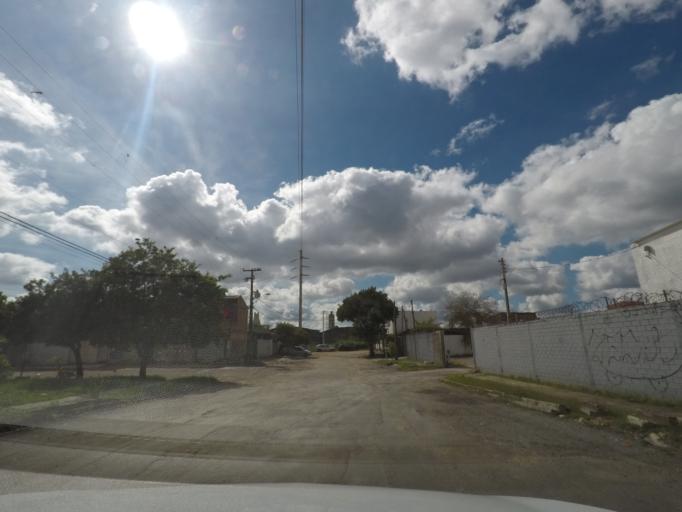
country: BR
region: Parana
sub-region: Sao Jose Dos Pinhais
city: Sao Jose dos Pinhais
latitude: -25.4933
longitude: -49.2290
